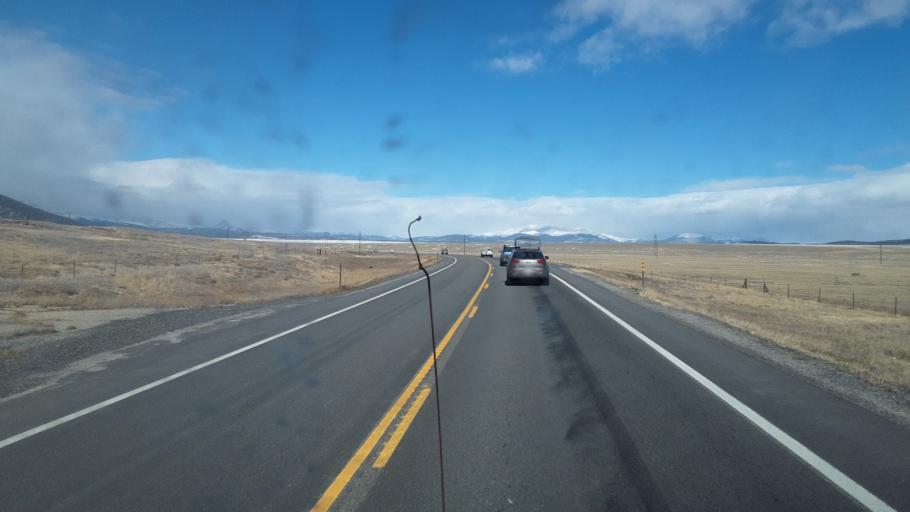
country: US
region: Colorado
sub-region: Park County
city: Fairplay
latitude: 39.0769
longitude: -105.9739
